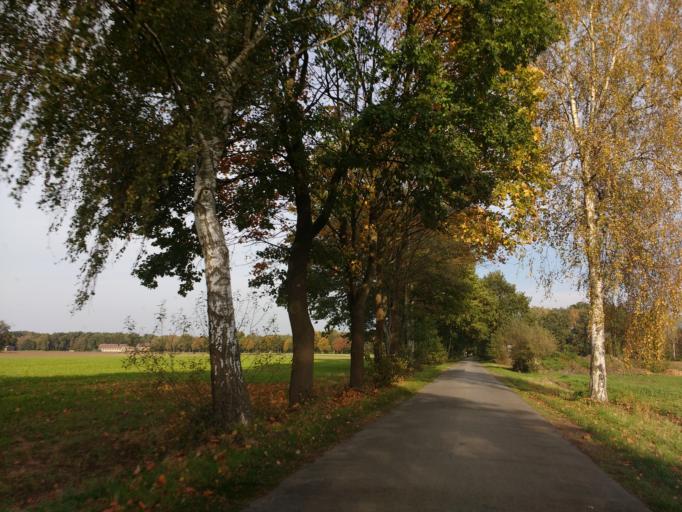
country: DE
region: North Rhine-Westphalia
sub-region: Regierungsbezirk Detmold
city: Hovelhof
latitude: 51.7728
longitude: 8.6617
